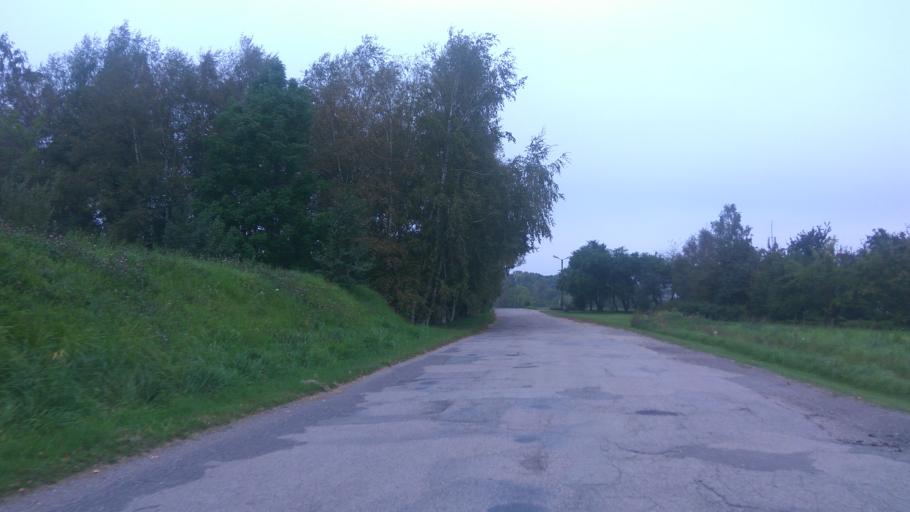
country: LV
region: Rucavas
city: Rucava
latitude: 56.1554
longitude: 21.1702
